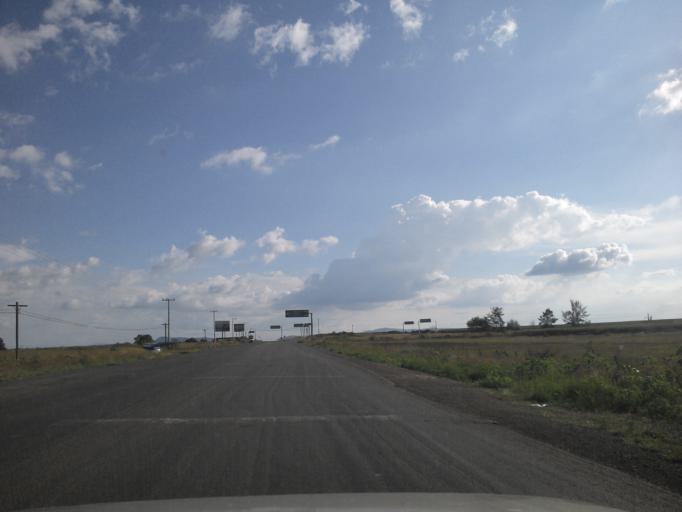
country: MX
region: Jalisco
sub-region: Atotonilco el Alto
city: Ojo de Agua de Moran
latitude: 20.5837
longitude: -102.4979
